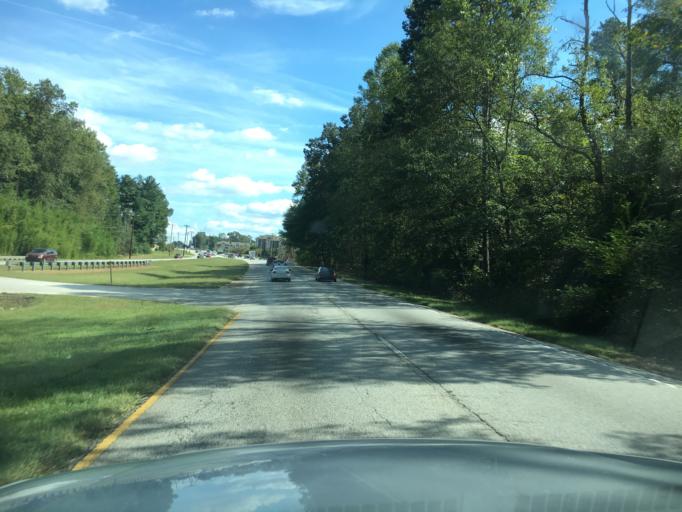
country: US
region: South Carolina
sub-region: Greenville County
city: Mauldin
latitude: 34.8064
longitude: -82.3280
